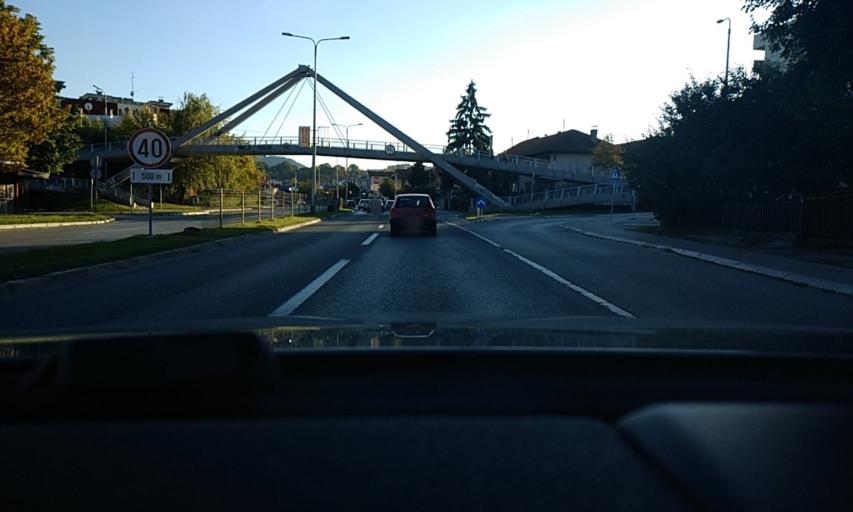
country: BA
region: Republika Srpska
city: Banja Luka
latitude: 44.7763
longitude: 17.1828
